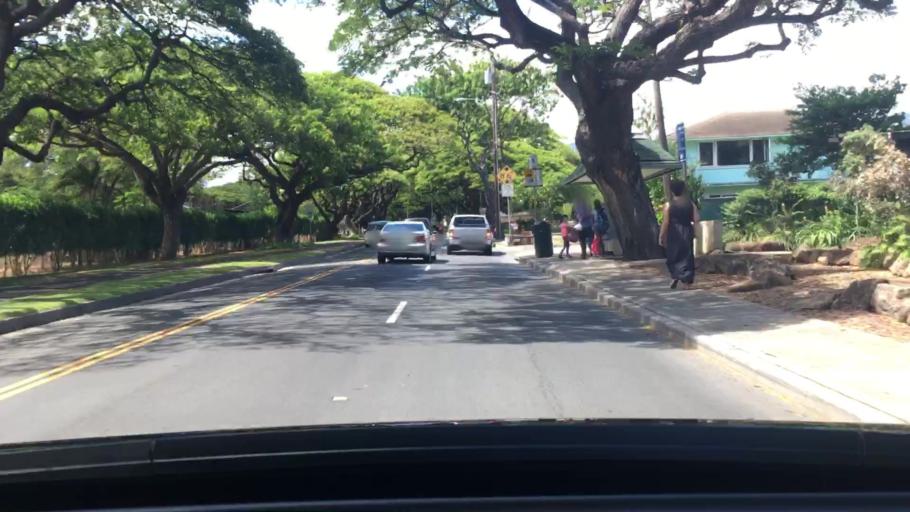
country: US
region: Hawaii
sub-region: Honolulu County
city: Honolulu
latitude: 21.2698
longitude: -157.8159
